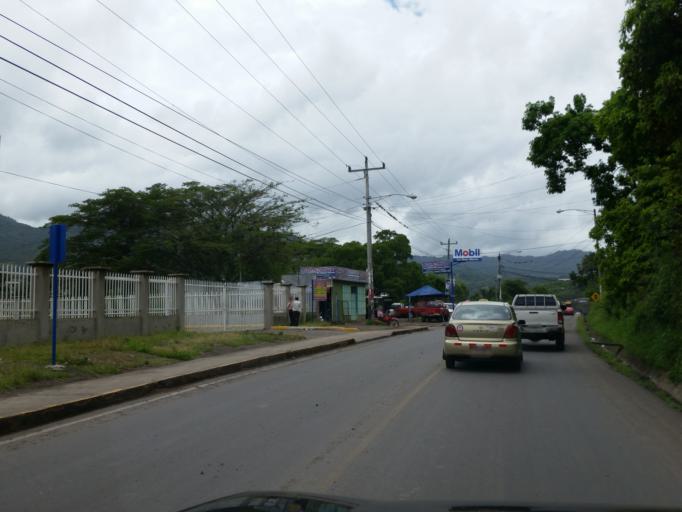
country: NI
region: Matagalpa
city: Matagalpa
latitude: 12.9355
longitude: -85.9201
